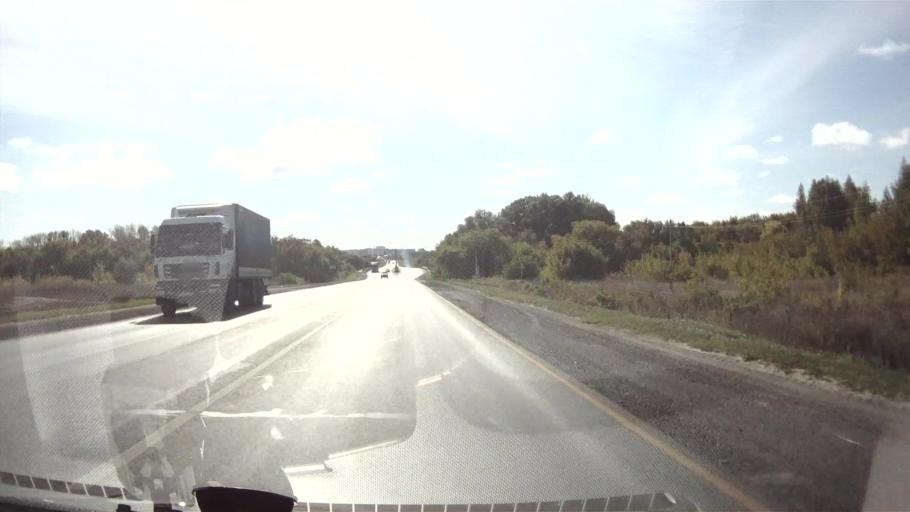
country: RU
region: Ulyanovsk
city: Isheyevka
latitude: 54.3061
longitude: 48.2401
